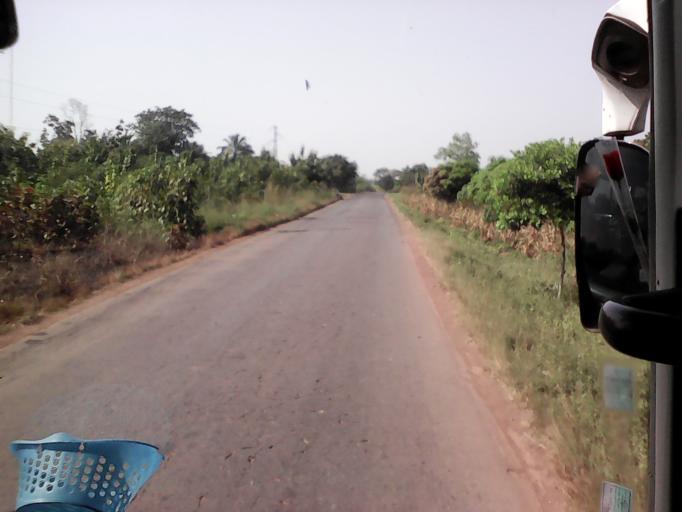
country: TG
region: Centrale
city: Sokode
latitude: 8.9099
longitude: 1.1001
